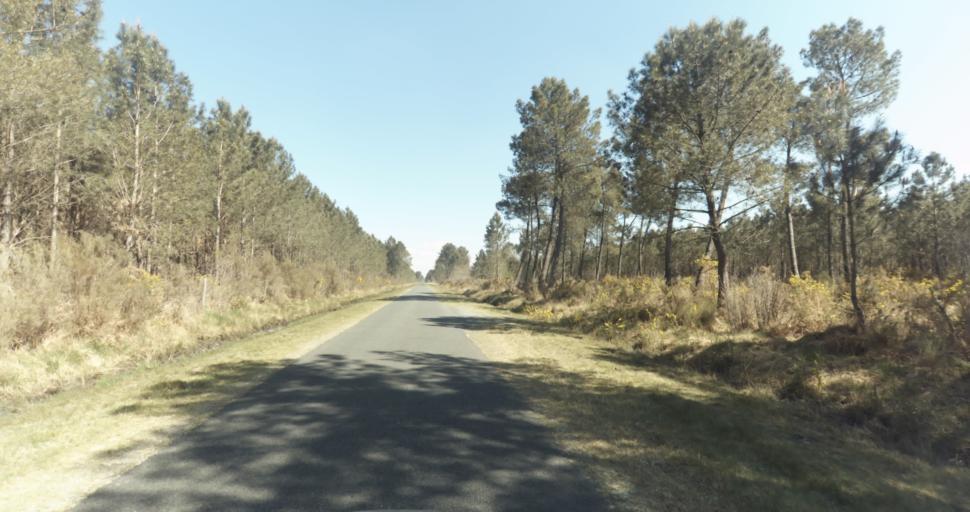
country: FR
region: Aquitaine
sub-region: Departement de la Gironde
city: Martignas-sur-Jalle
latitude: 44.7822
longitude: -0.8014
